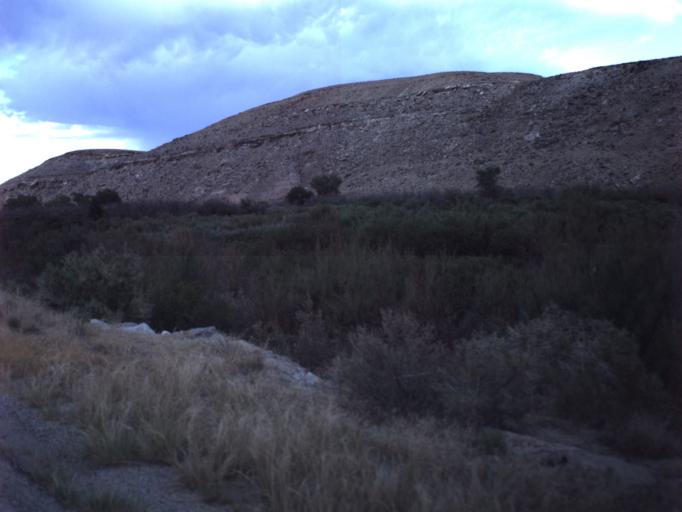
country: US
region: Utah
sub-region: Grand County
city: Moab
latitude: 38.8367
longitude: -109.2872
